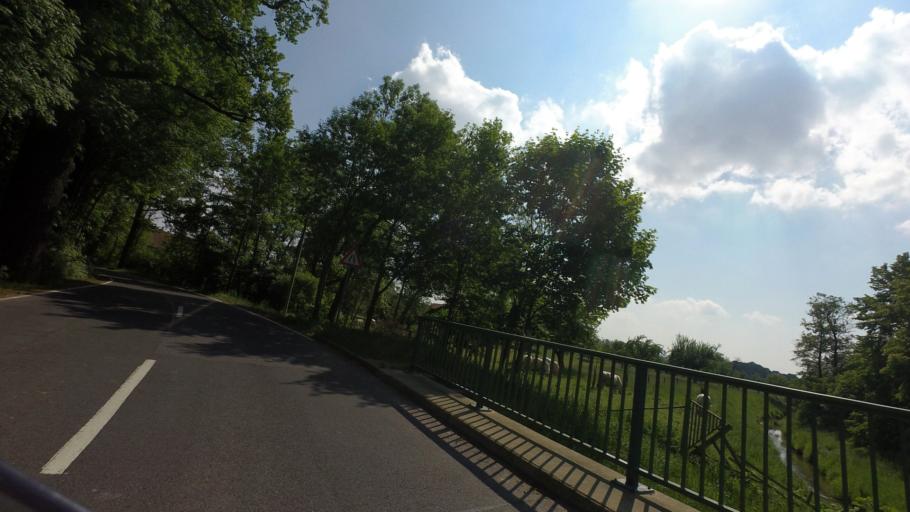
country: DE
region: Saxony
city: Hochkirch
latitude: 51.1964
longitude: 14.5990
